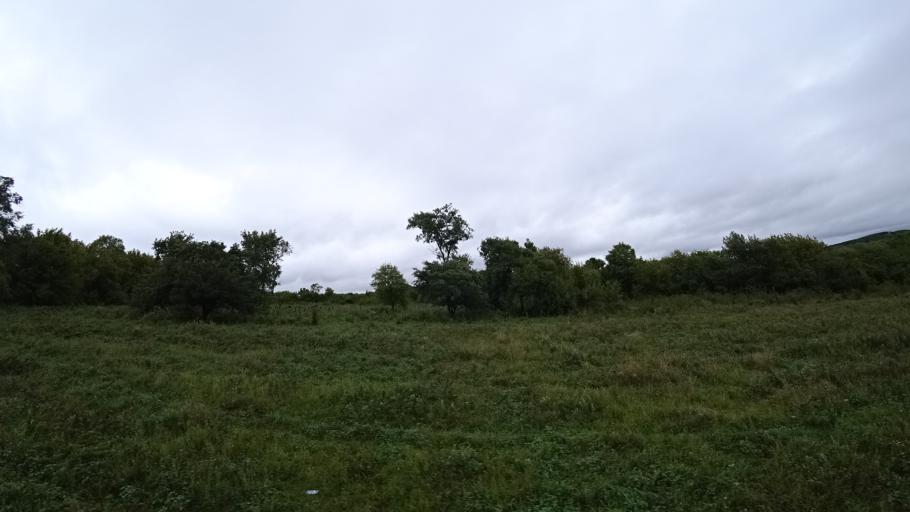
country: RU
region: Primorskiy
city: Monastyrishche
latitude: 44.2639
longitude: 132.4222
